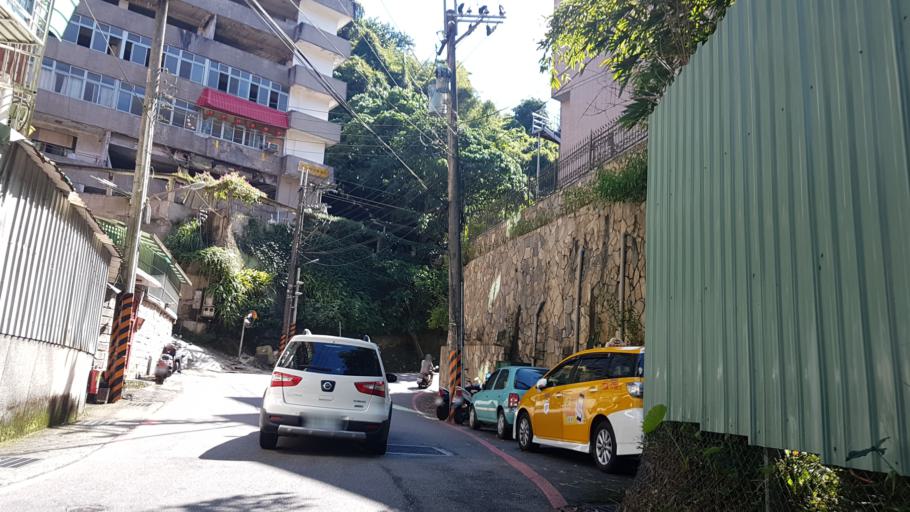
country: TW
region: Taipei
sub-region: Taipei
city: Banqiao
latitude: 24.9546
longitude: 121.5318
